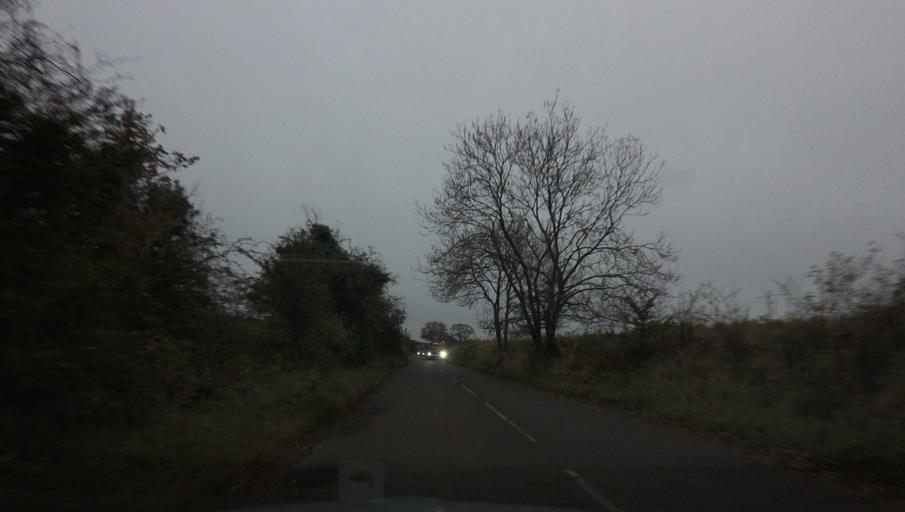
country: GB
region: Scotland
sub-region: Fife
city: Crossford
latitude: 56.0425
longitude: -3.5058
